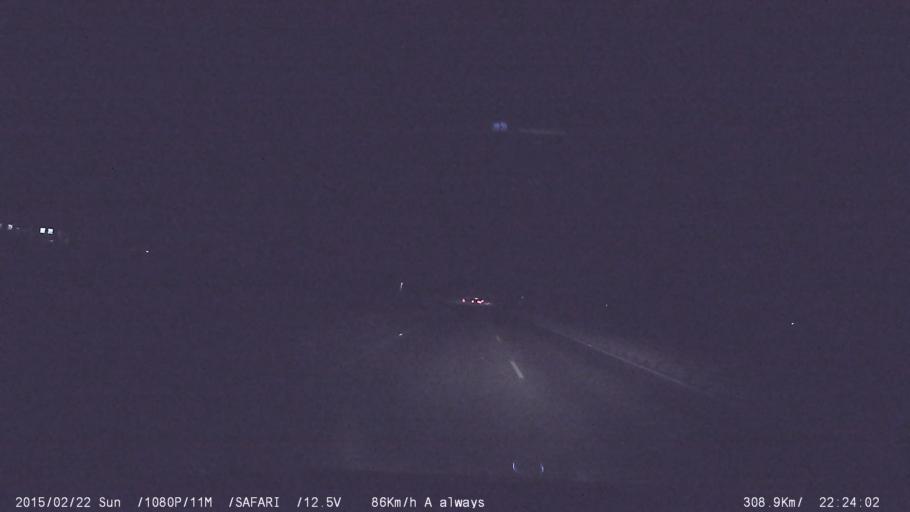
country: IN
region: Tamil Nadu
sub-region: Karur
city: Karur
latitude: 11.0327
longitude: 78.0636
